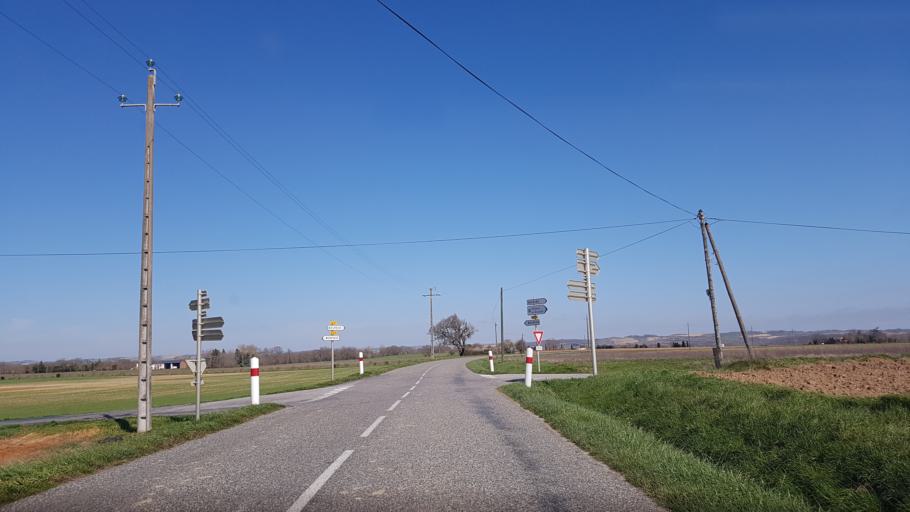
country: FR
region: Languedoc-Roussillon
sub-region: Departement de l'Aude
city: Belpech
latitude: 43.1804
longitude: 1.7119
